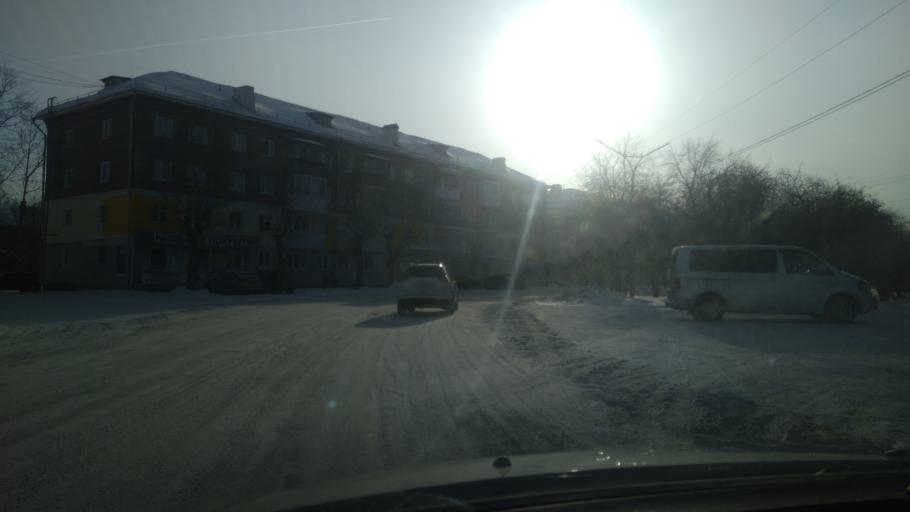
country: RU
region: Sverdlovsk
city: Sukhoy Log
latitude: 56.9085
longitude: 62.0341
